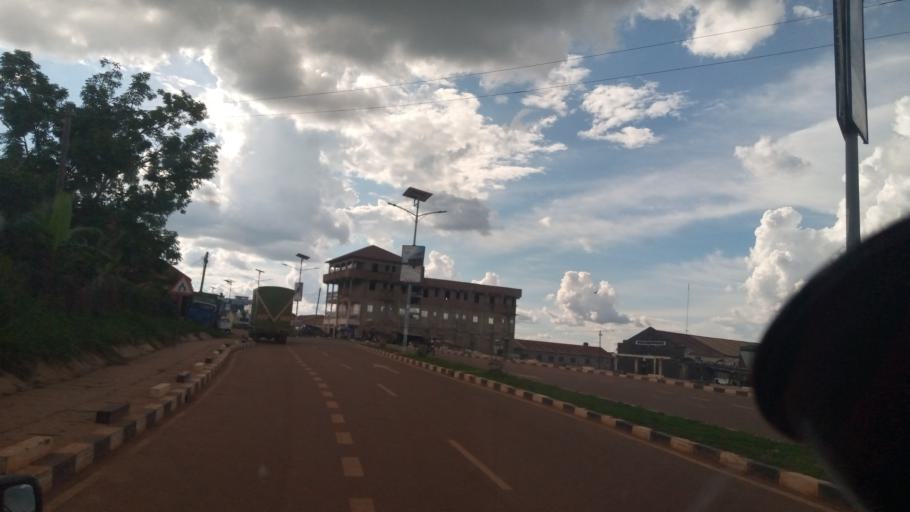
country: UG
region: Northern Region
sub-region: Lira District
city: Lira
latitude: 2.2410
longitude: 32.8993
